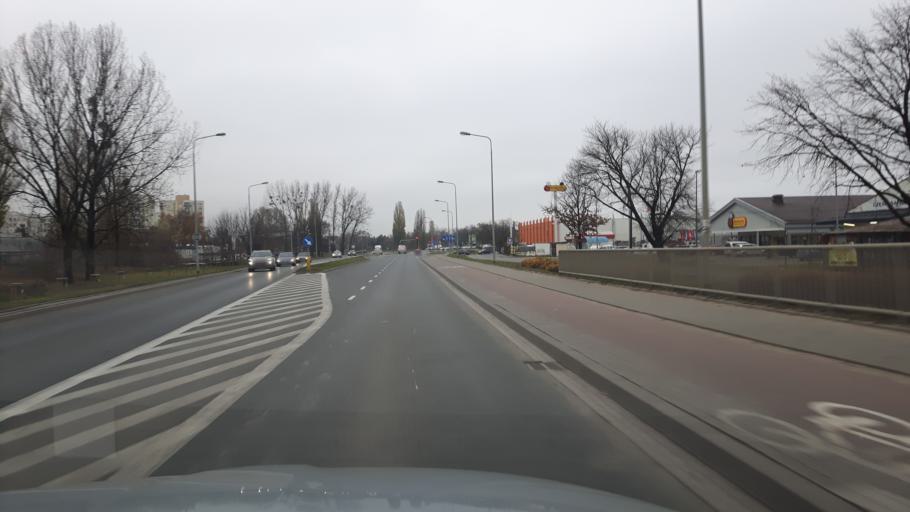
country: PL
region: Masovian Voivodeship
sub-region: Warszawa
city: Targowek
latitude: 52.2726
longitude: 21.0688
